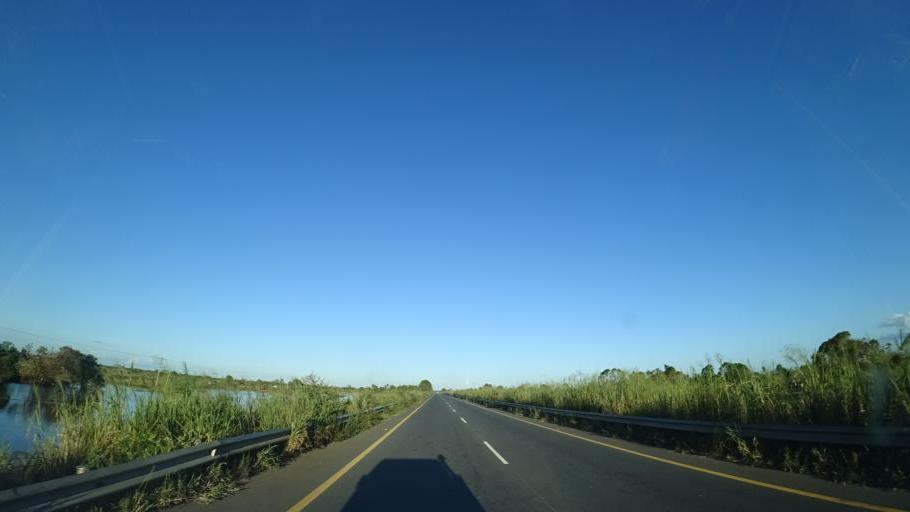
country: MZ
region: Sofala
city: Dondo
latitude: -19.3372
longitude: 34.3315
